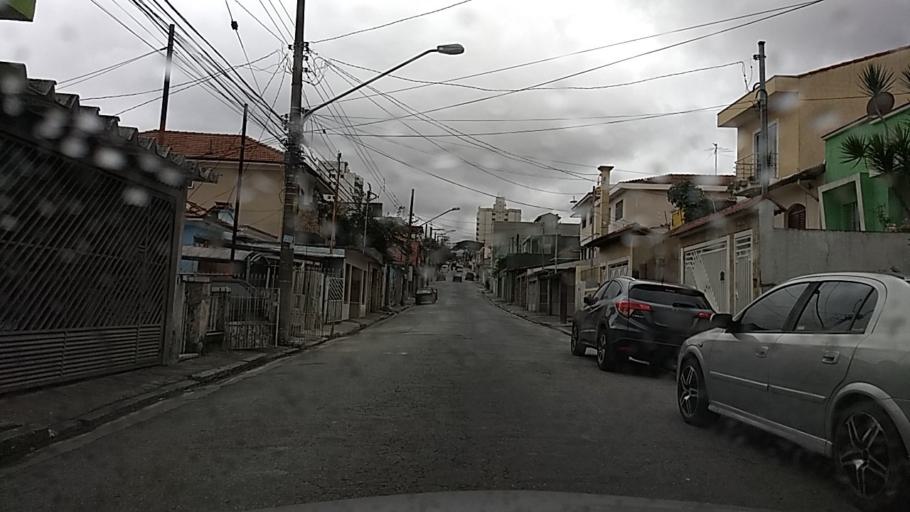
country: BR
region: Sao Paulo
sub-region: Sao Paulo
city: Sao Paulo
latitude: -23.5038
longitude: -46.5969
